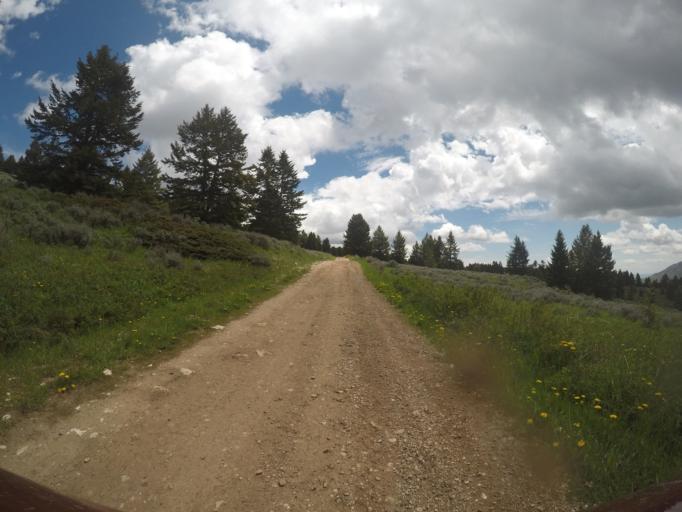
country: US
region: Wyoming
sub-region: Big Horn County
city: Lovell
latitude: 45.1706
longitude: -108.4292
